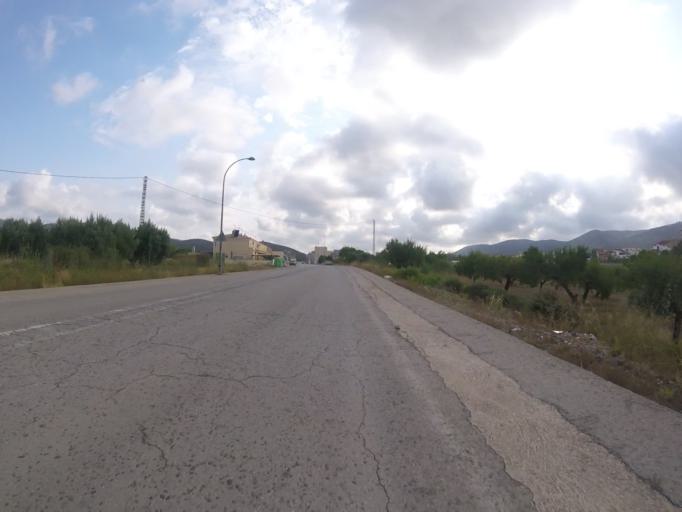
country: ES
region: Valencia
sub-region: Provincia de Castello
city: Santa Magdalena de Pulpis
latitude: 40.3565
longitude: 0.2992
